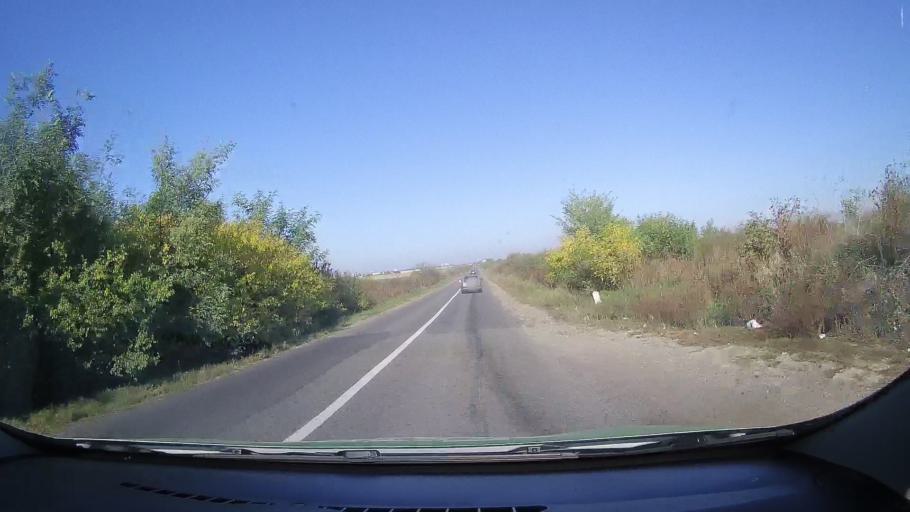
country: RO
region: Satu Mare
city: Carei
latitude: 47.6629
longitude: 22.4924
